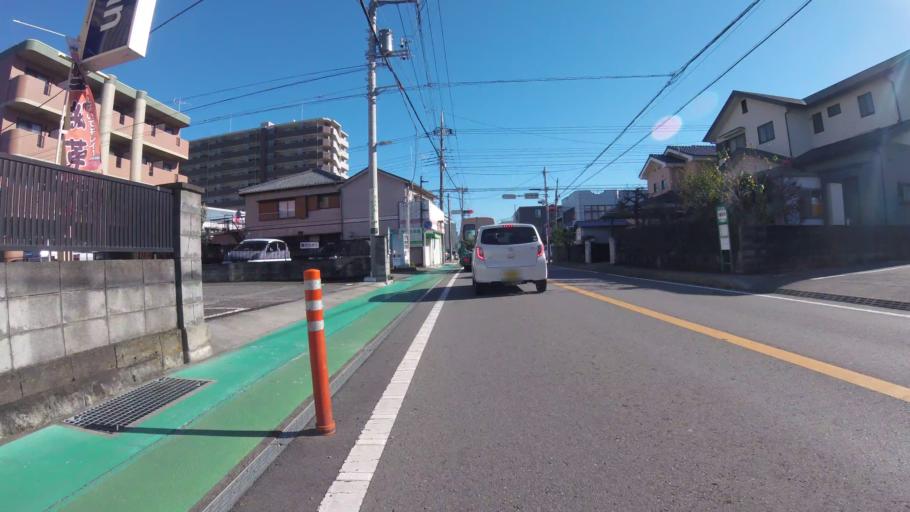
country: JP
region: Shizuoka
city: Mishima
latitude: 35.1199
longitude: 138.9003
